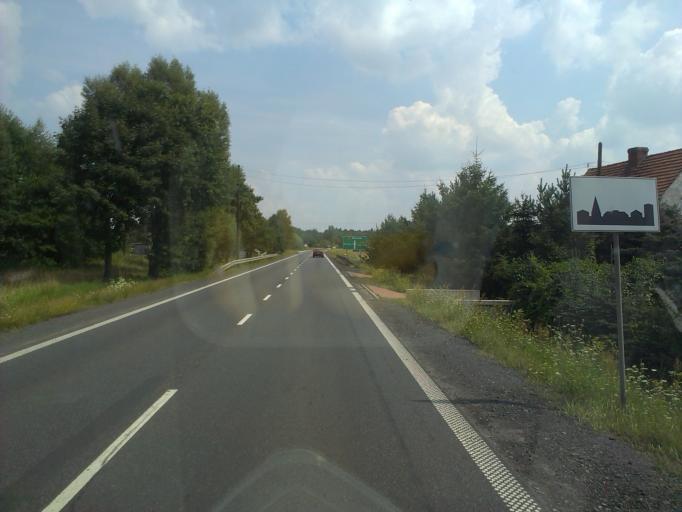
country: PL
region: Lower Silesian Voivodeship
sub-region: Powiat sredzki
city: Malczyce
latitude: 51.1956
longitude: 16.4977
